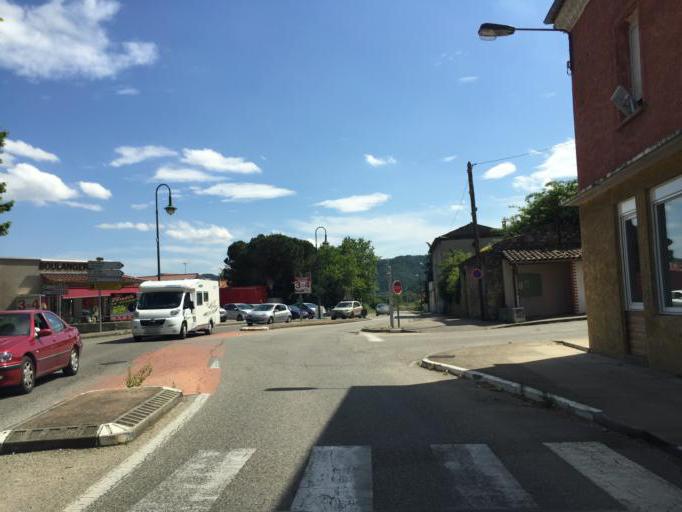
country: FR
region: Rhone-Alpes
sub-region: Departement de la Drome
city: Saint-Vallier
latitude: 45.1398
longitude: 4.8072
